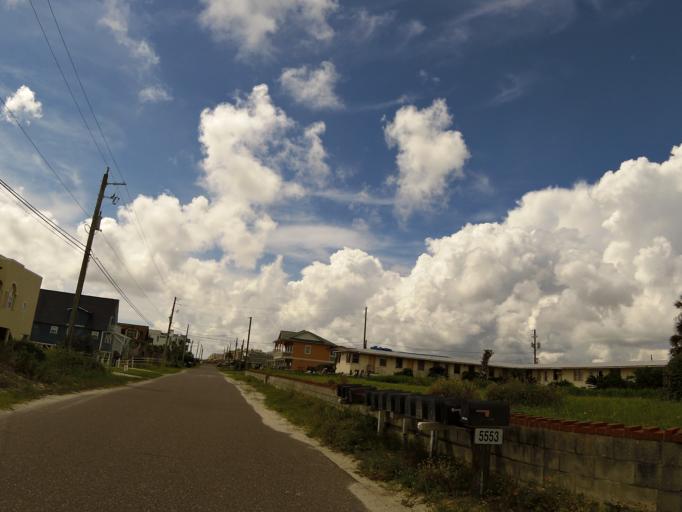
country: US
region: Florida
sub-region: Nassau County
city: Fernandina Beach
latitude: 30.5722
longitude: -81.4443
